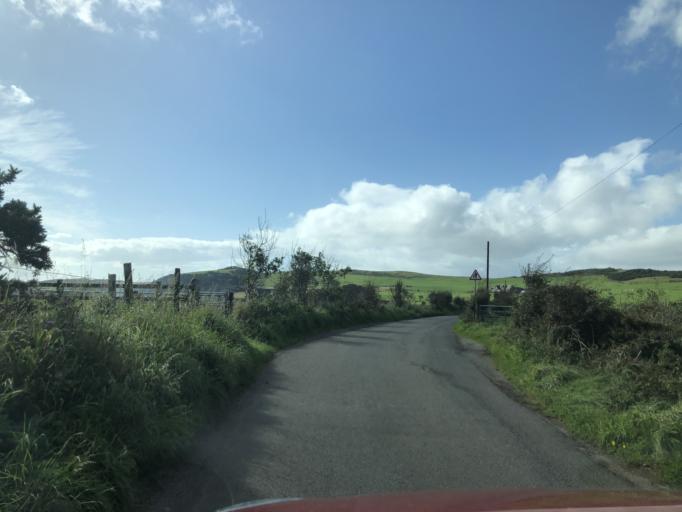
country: GB
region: Scotland
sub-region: Argyll and Bute
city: Campbeltown
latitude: 55.3233
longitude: -5.6274
